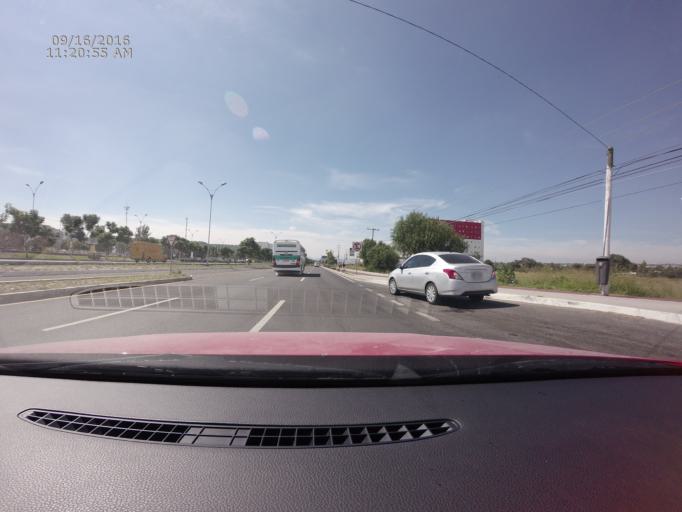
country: MX
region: Queretaro
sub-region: Queretaro
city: El Salitre
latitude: 20.6717
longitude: -100.4342
